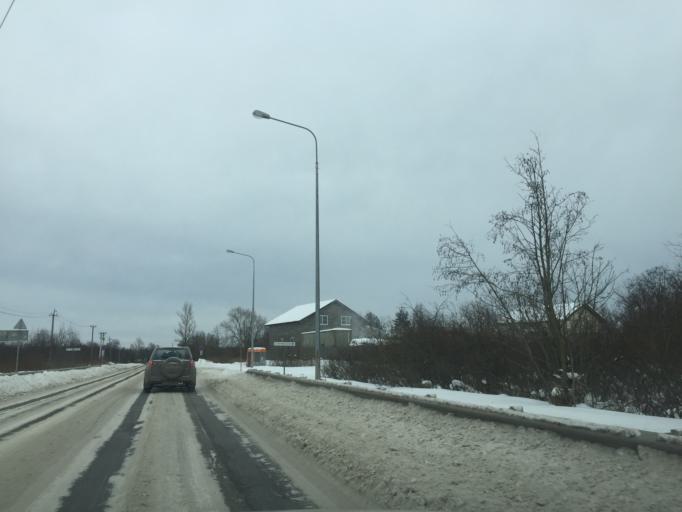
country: RU
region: Leningrad
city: Imeni Sverdlova
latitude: 59.7963
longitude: 30.6665
